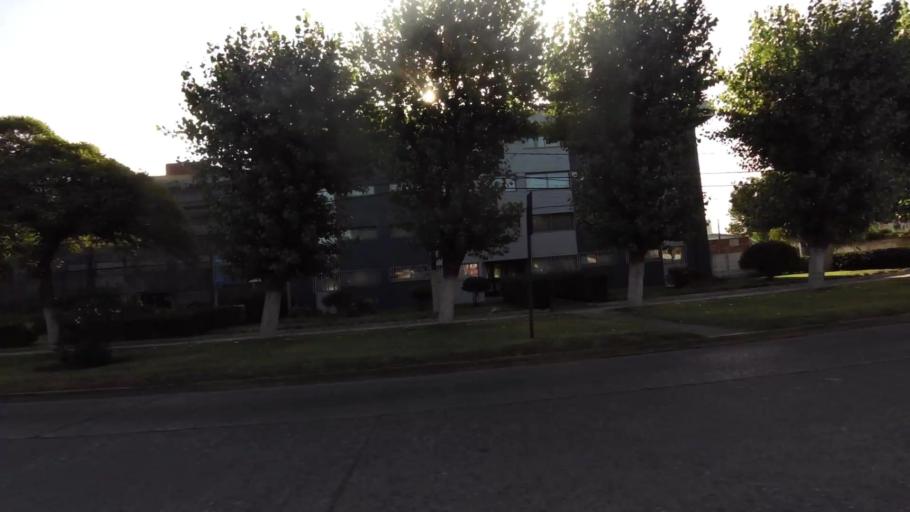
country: CL
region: Biobio
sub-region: Provincia de Concepcion
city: Concepcion
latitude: -36.7886
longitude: -73.0869
